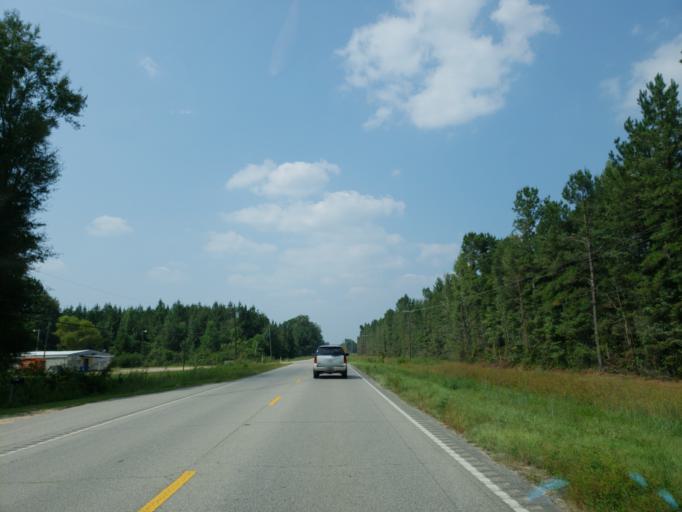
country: US
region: Mississippi
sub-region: Forrest County
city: Glendale
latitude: 31.4292
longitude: -89.2824
